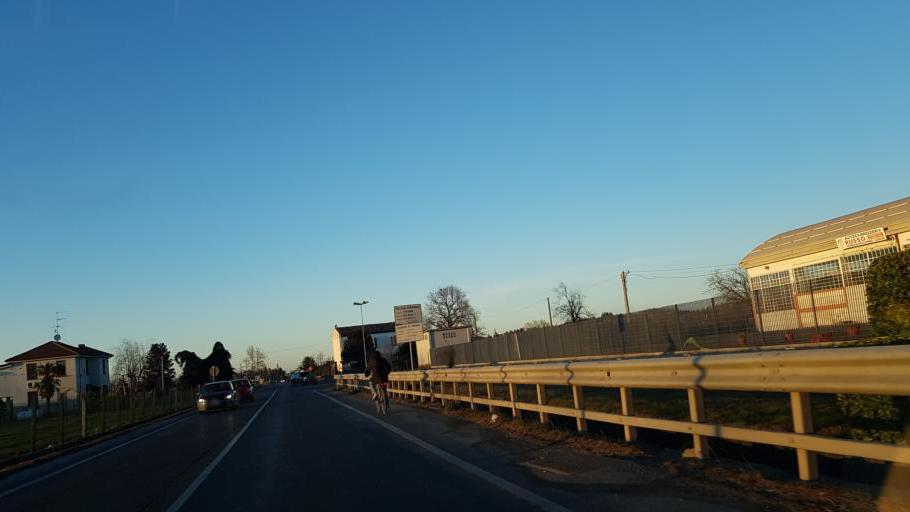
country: IT
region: Piedmont
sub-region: Provincia di Alessandria
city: Carbonara Scrivia
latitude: 44.8657
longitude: 8.8561
